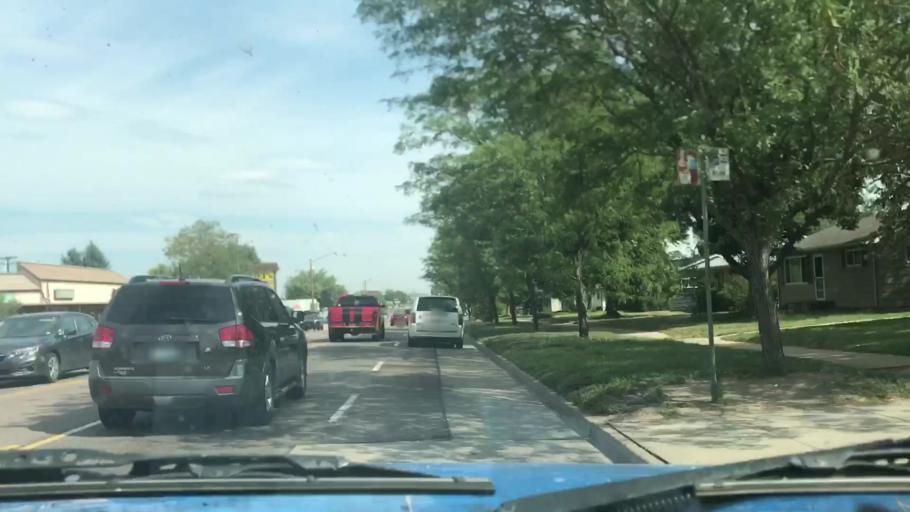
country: US
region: Colorado
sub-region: Jefferson County
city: Lakewood
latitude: 39.7152
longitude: -105.0532
